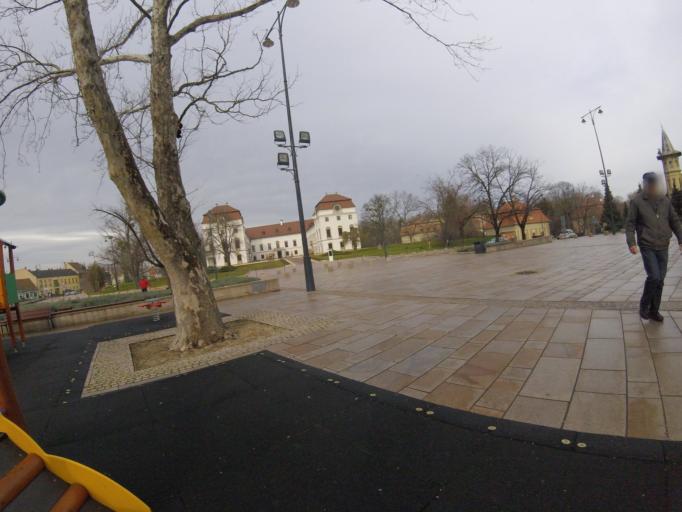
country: HU
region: Veszprem
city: Papa
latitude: 47.3314
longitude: 17.4652
